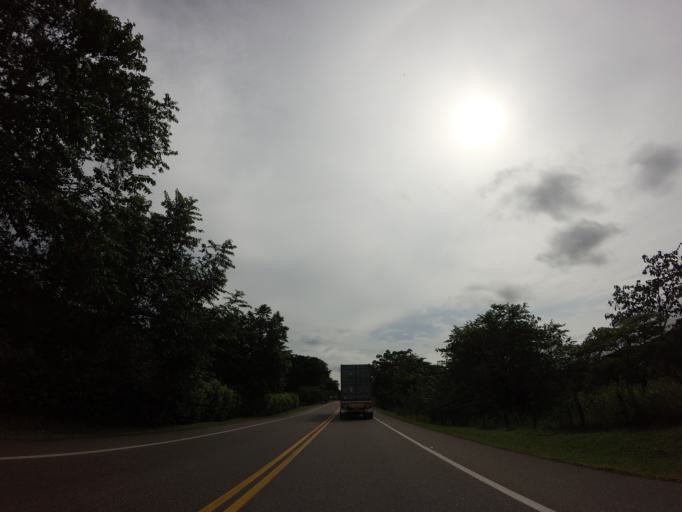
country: CO
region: Caldas
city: La Dorada
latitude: 5.4146
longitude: -74.6882
